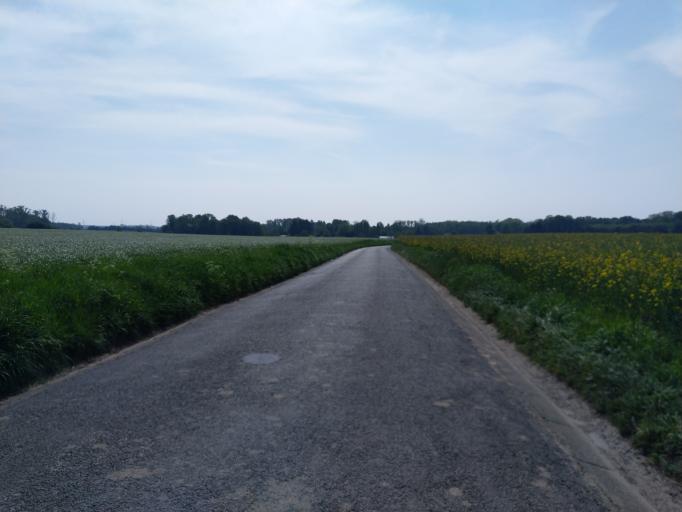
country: BE
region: Wallonia
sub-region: Province du Hainaut
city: Estinnes-au-Val
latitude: 50.4531
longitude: 4.0349
